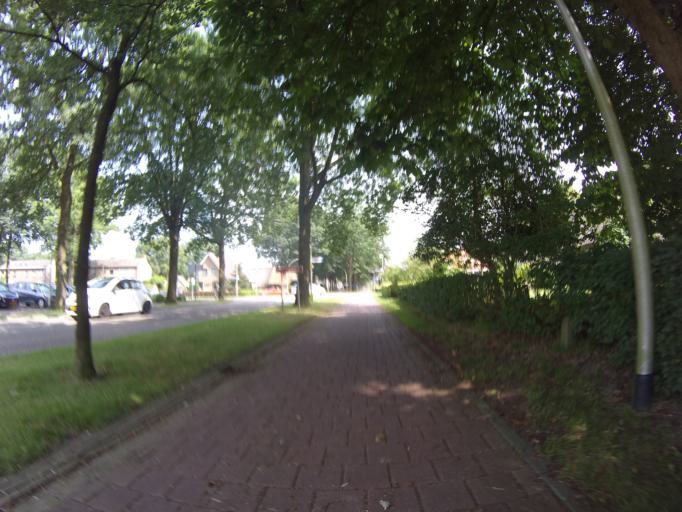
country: NL
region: Drenthe
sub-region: Gemeente Coevorden
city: Sleen
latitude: 52.7878
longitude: 6.7166
